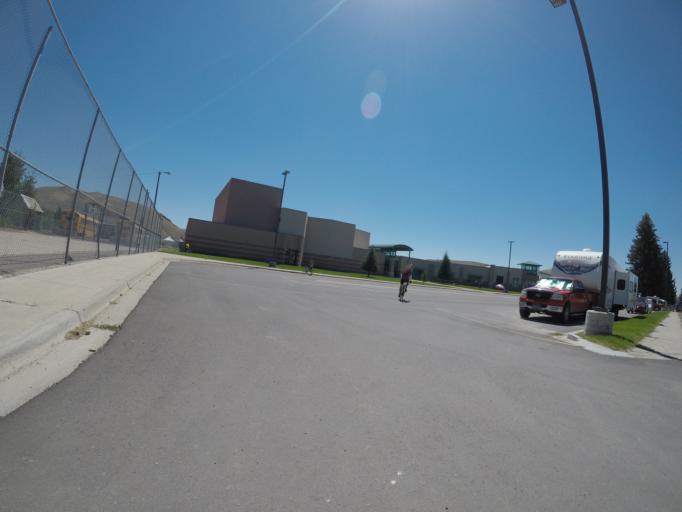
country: US
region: Idaho
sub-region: Bear Lake County
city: Montpelier
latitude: 42.0837
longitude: -110.9563
